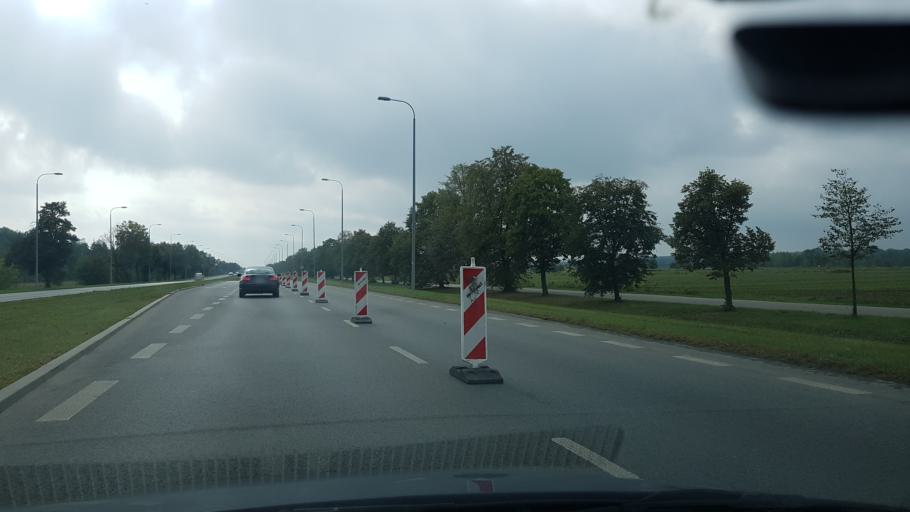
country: PL
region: Masovian Voivodeship
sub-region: Warszawa
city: Wilanow
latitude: 52.1459
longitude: 21.0941
